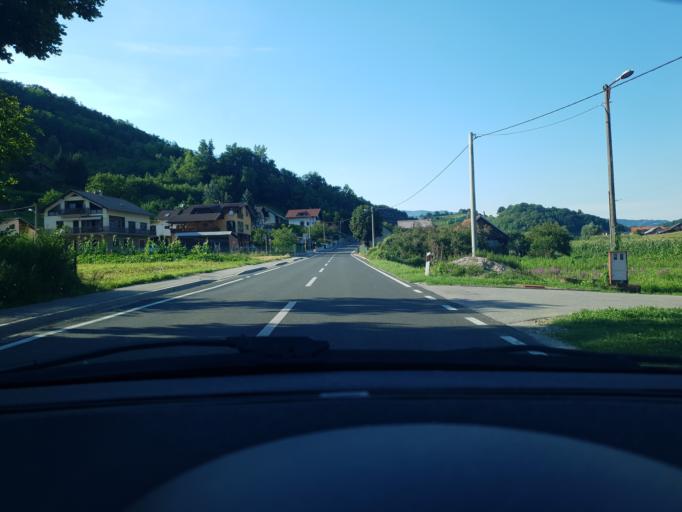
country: HR
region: Krapinsko-Zagorska
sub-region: Grad Krapina
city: Krapina
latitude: 46.1109
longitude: 15.9061
